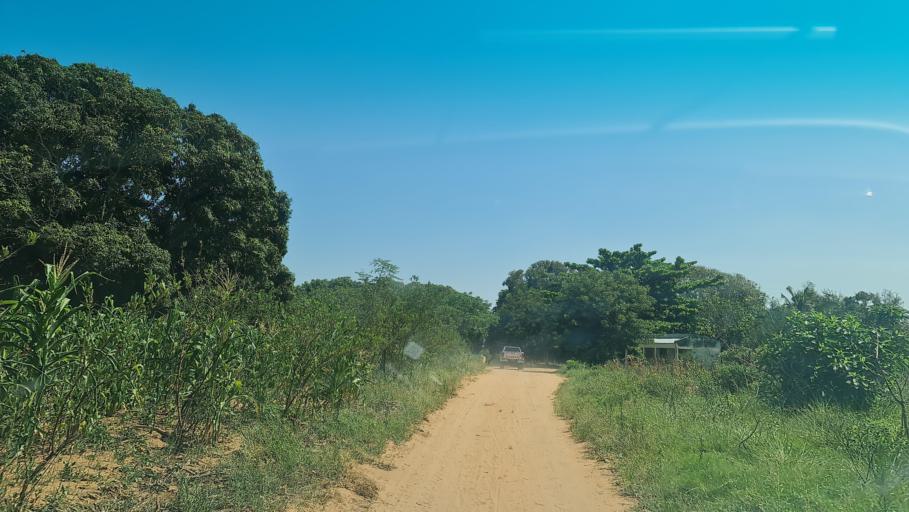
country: MZ
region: Gaza
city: Macia
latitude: -25.0870
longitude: 33.0987
